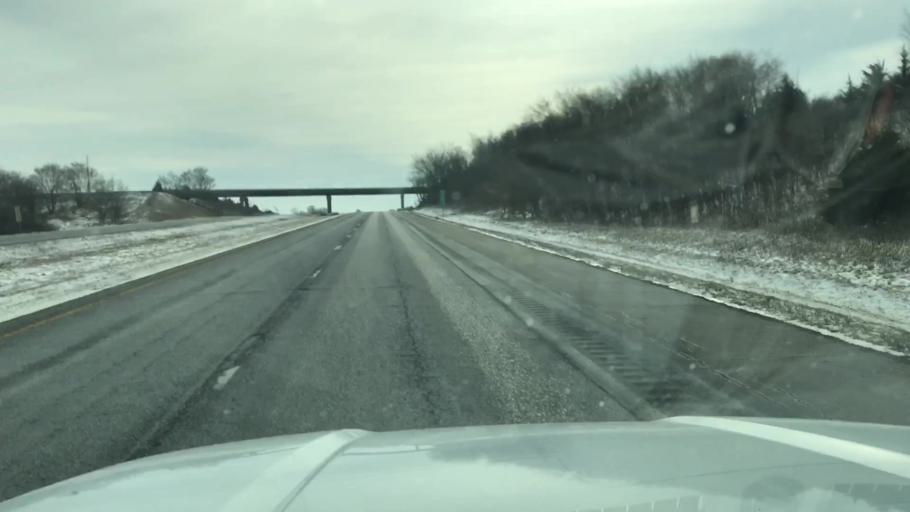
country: US
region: Missouri
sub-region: Holt County
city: Oregon
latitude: 40.0157
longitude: -95.0872
